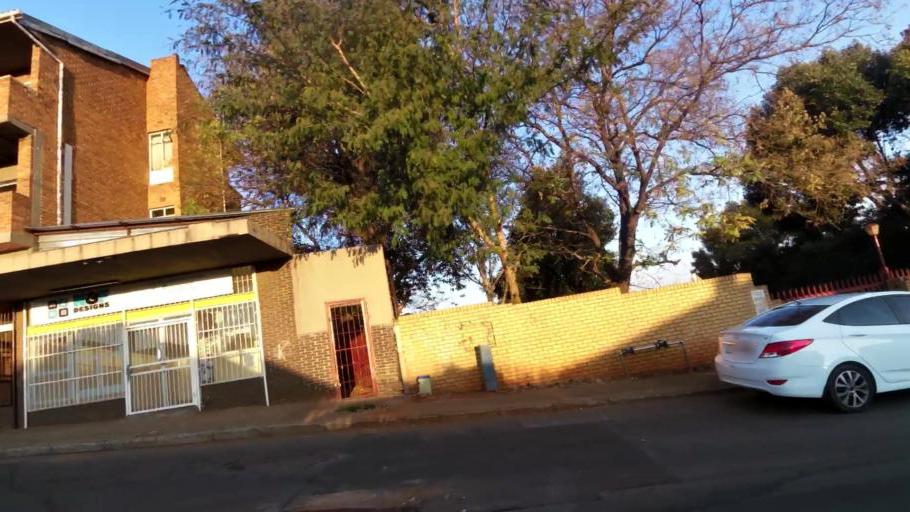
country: ZA
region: Gauteng
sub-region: City of Johannesburg Metropolitan Municipality
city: Roodepoort
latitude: -26.1845
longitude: 27.9503
